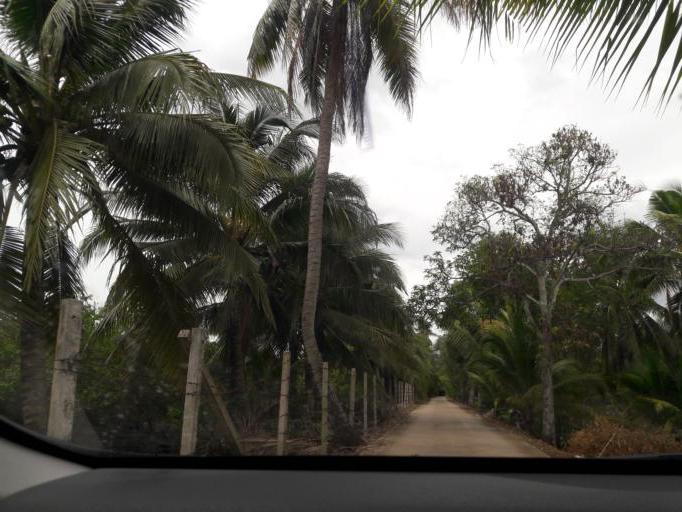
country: TH
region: Ratchaburi
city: Damnoen Saduak
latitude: 13.5651
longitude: 99.9899
